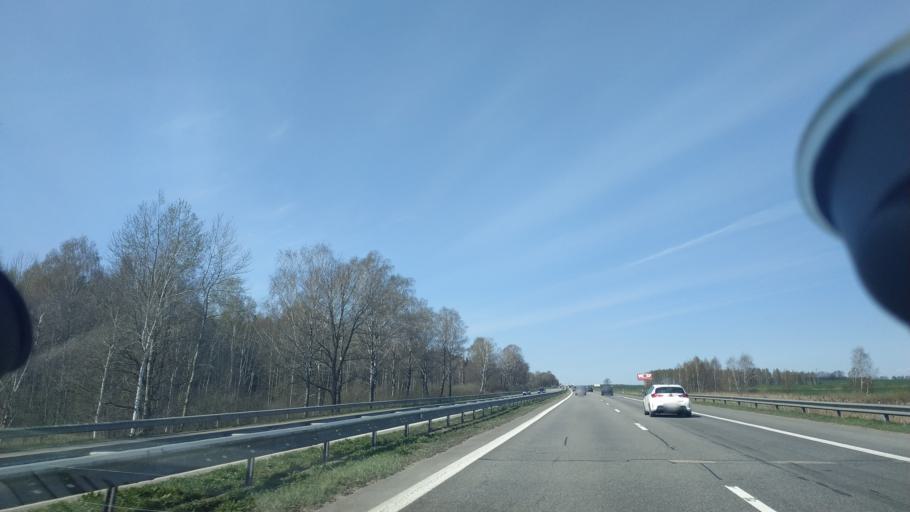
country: LT
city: Kaisiadorys
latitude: 54.8487
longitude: 24.3174
